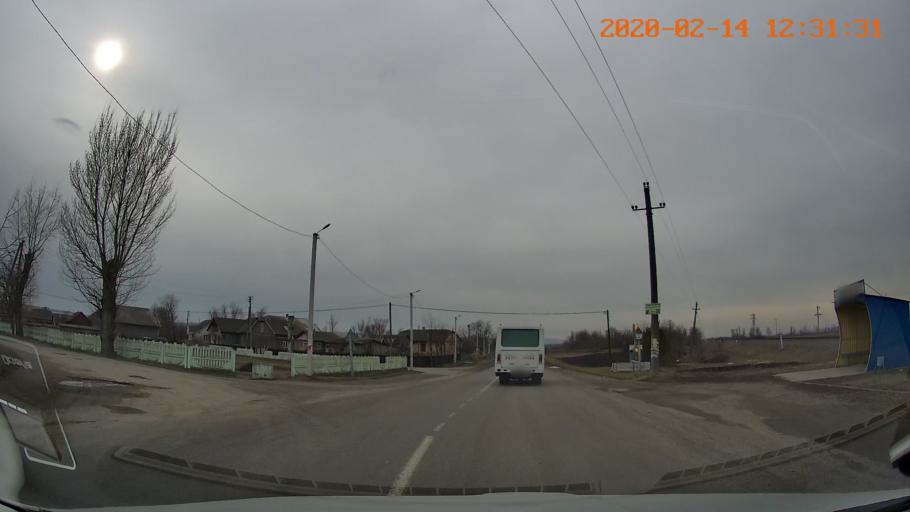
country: RO
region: Botosani
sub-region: Comuna Darabani
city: Bajura
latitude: 48.2482
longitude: 26.5567
